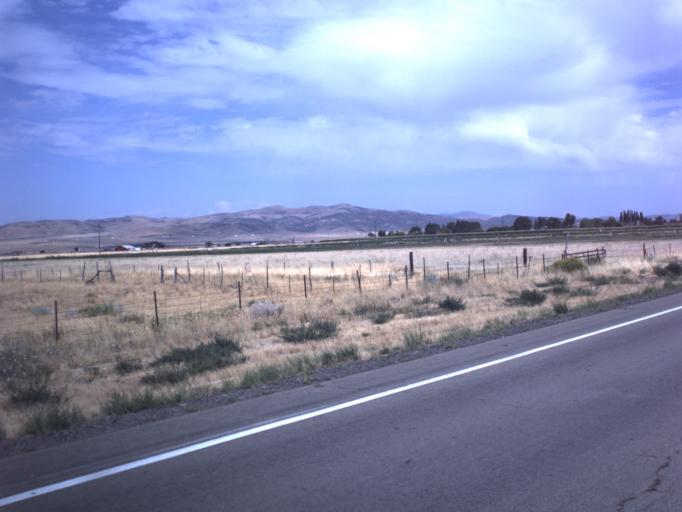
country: US
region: Utah
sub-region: Juab County
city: Nephi
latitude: 39.5433
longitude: -111.8637
